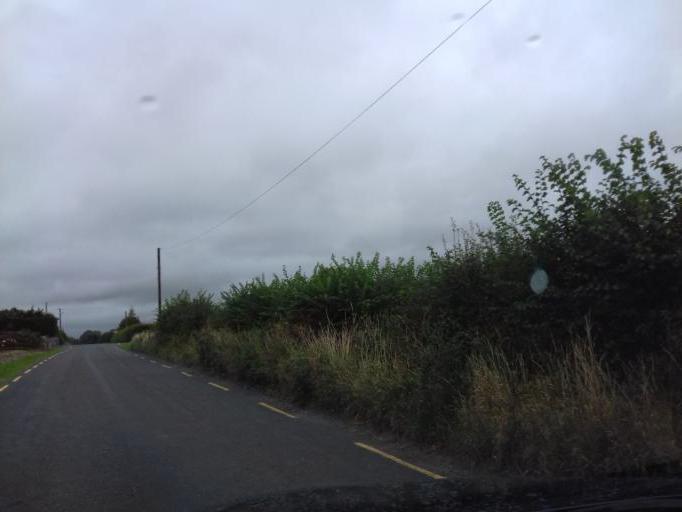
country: IE
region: Leinster
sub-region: Kilkenny
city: Graiguenamanagh
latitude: 52.6129
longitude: -7.0323
